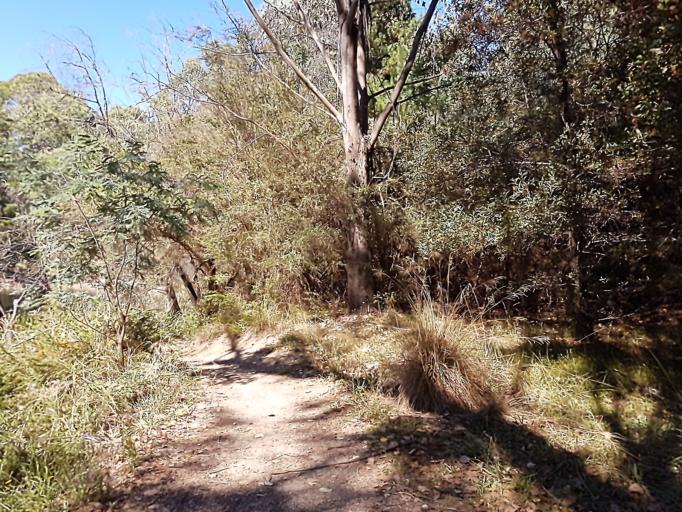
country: AU
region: Victoria
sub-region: Alpine
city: Mount Beauty
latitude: -36.8964
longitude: 147.0697
